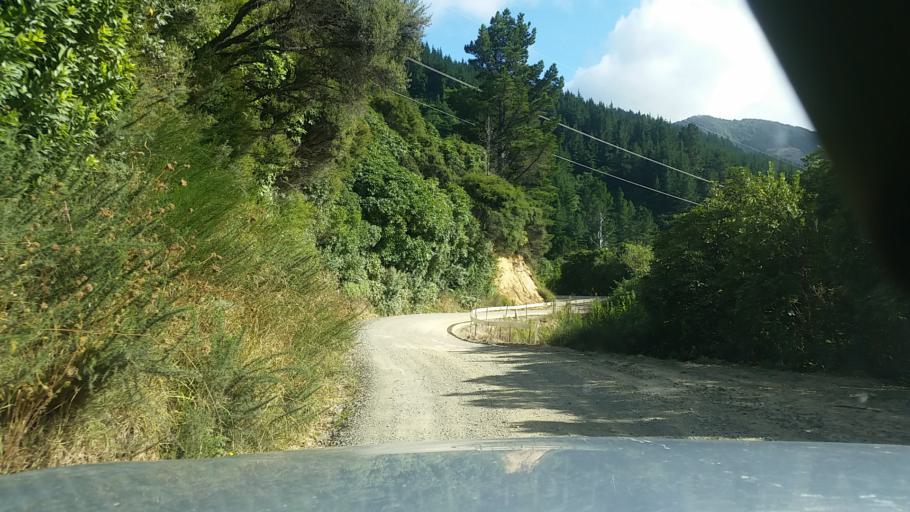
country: NZ
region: Marlborough
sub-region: Marlborough District
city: Picton
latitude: -41.2921
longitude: 174.1301
